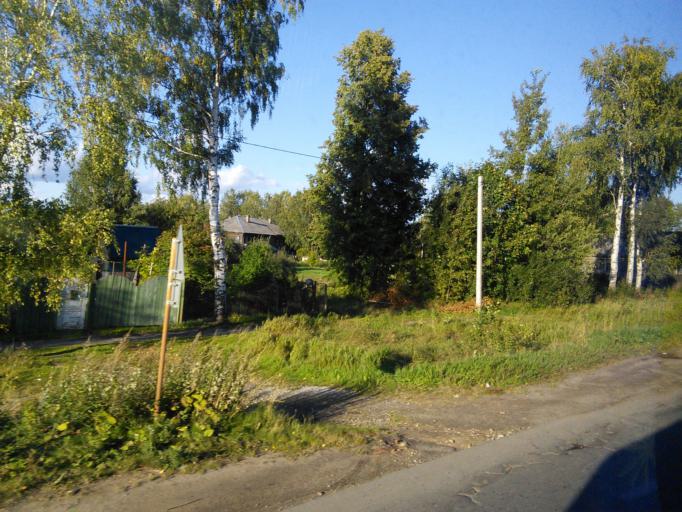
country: RU
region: Jaroslavl
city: Poshekhon'ye
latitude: 58.4978
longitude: 39.1173
